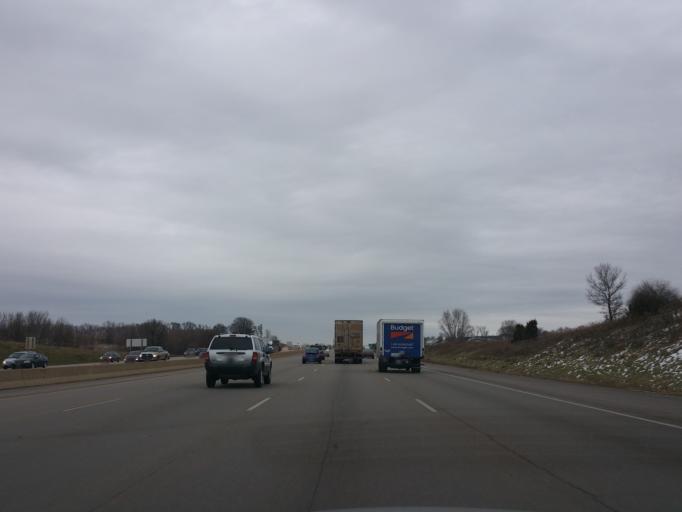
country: US
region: Wisconsin
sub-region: Dane County
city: Monona
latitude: 43.1196
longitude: -89.2888
